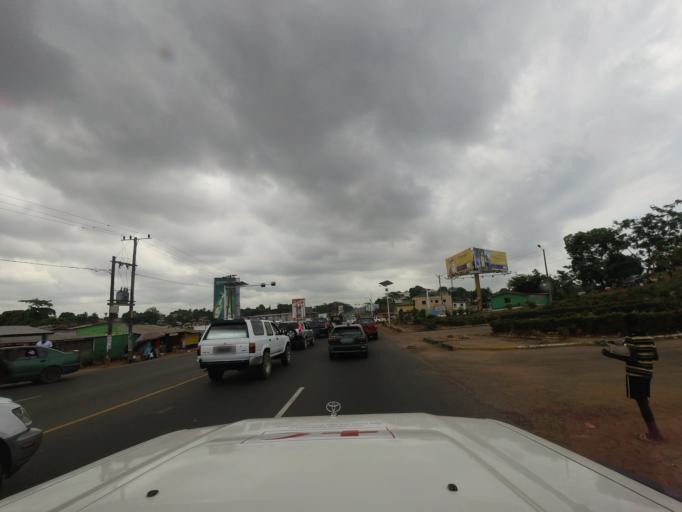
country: LR
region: Montserrado
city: Monrovia
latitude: 6.2644
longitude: -10.7141
